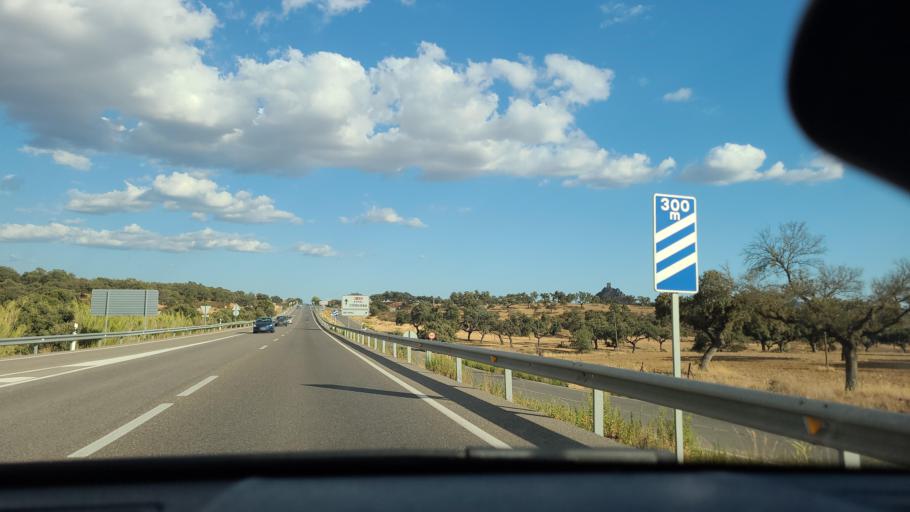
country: ES
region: Andalusia
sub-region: Province of Cordoba
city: Belmez
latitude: 38.2901
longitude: -5.2263
